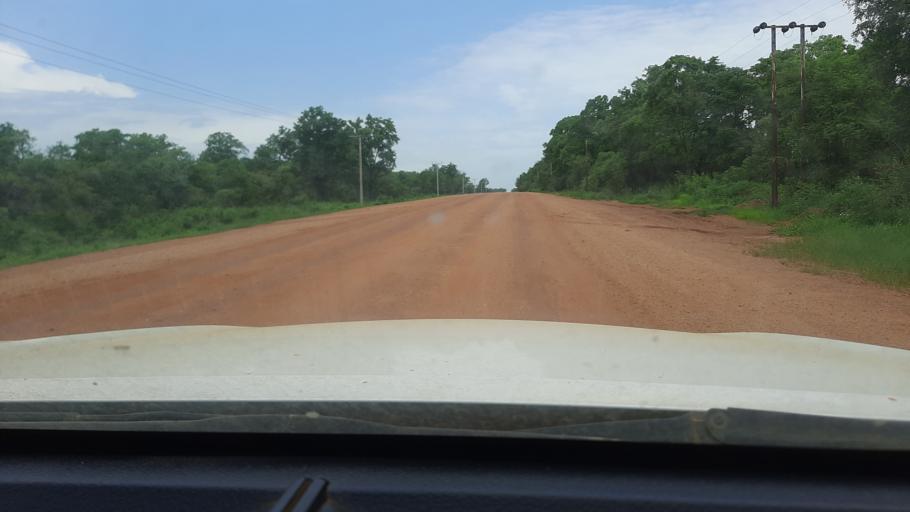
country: ET
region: Gambela
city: Gambela
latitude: 8.1348
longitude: 34.5787
